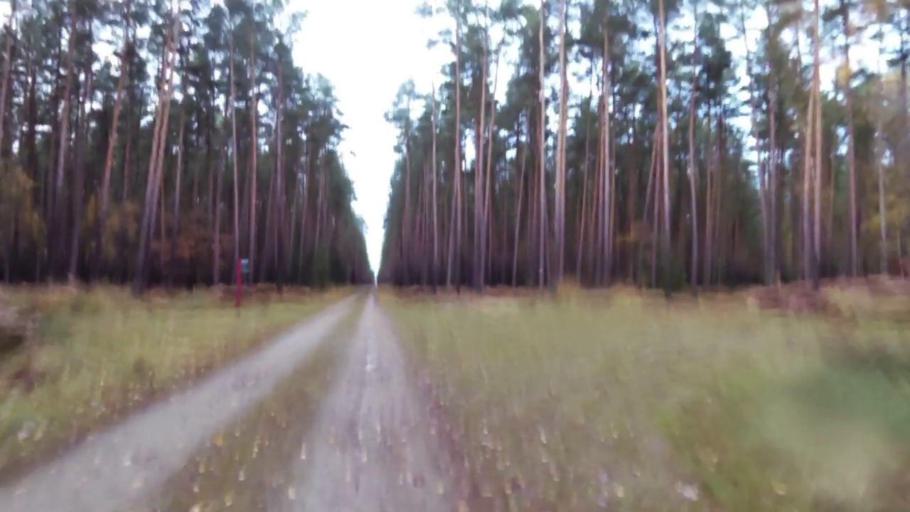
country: PL
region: West Pomeranian Voivodeship
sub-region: Powiat goleniowski
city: Stepnica
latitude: 53.6362
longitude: 14.7119
